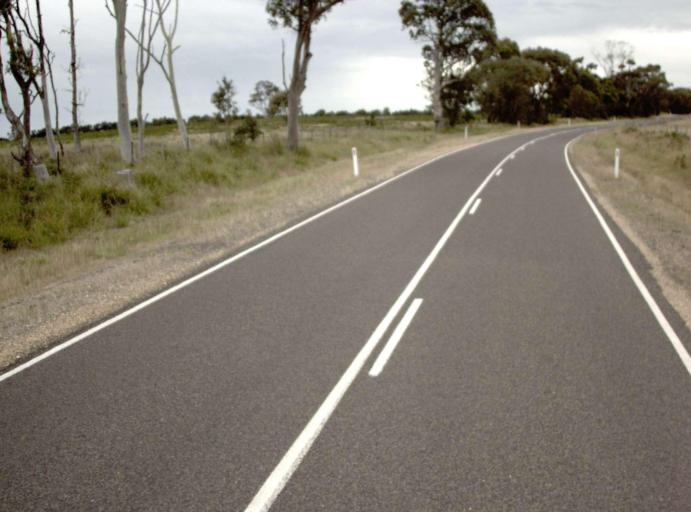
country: AU
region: Victoria
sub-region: East Gippsland
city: Bairnsdale
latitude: -37.9692
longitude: 147.4778
